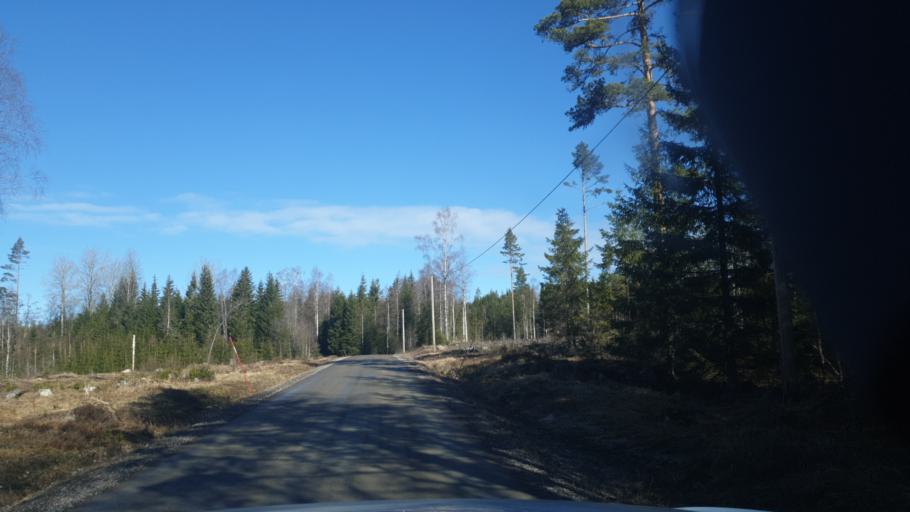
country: NO
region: Ostfold
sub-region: Romskog
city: Romskog
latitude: 59.7033
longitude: 12.0539
